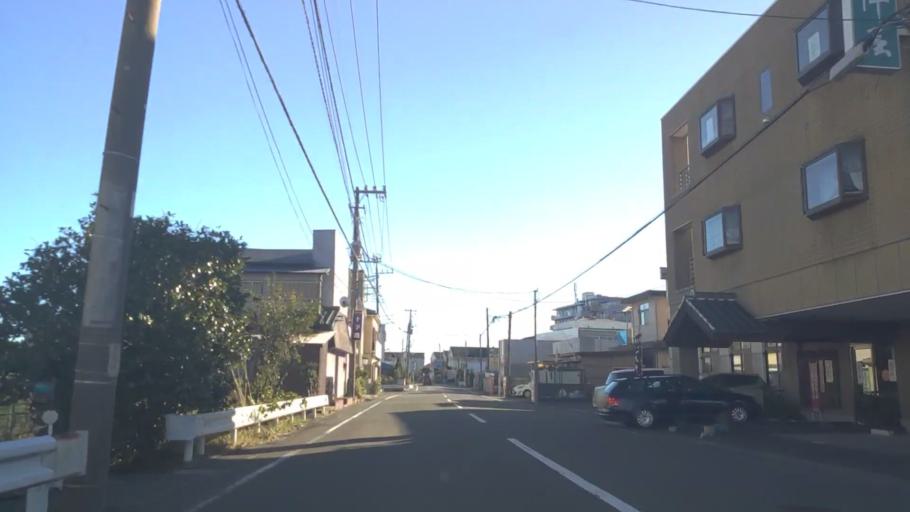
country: JP
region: Kanagawa
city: Atsugi
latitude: 35.3829
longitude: 139.3651
